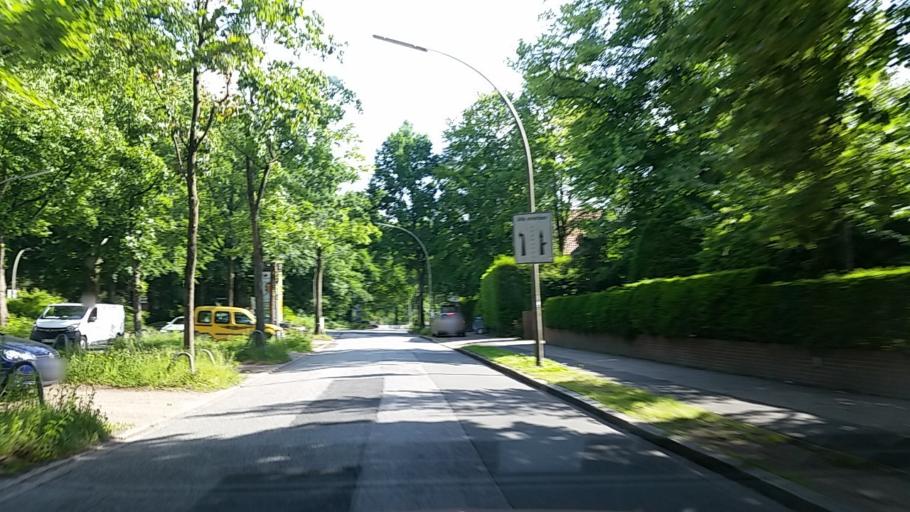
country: DE
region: Hamburg
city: Eidelstedt
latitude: 53.5636
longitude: 9.8870
